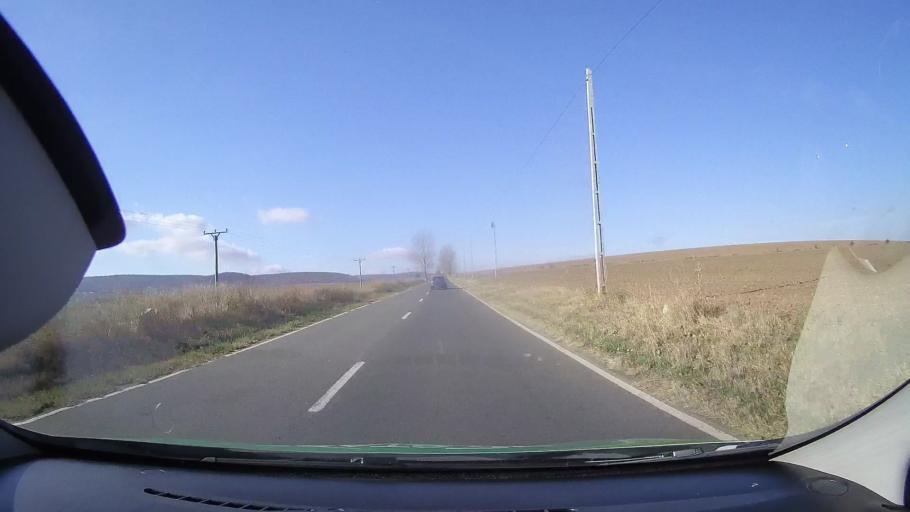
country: RO
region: Tulcea
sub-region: Comuna Sarichioi
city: Enisala
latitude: 44.8790
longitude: 28.7924
